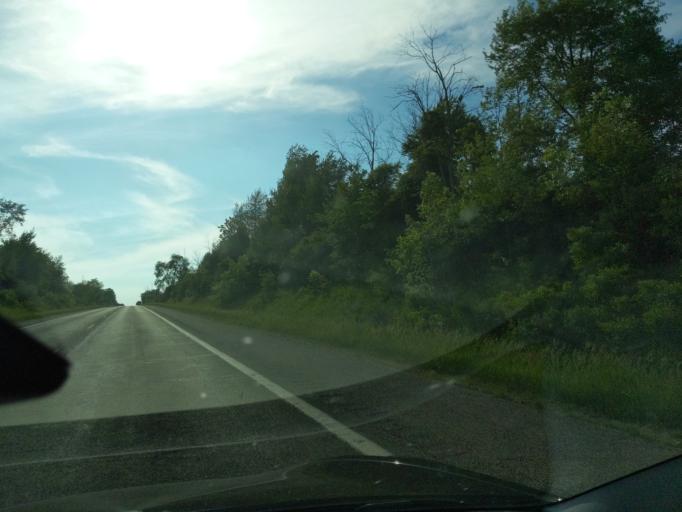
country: US
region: Michigan
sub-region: Barry County
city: Nashville
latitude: 42.6034
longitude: -85.1269
